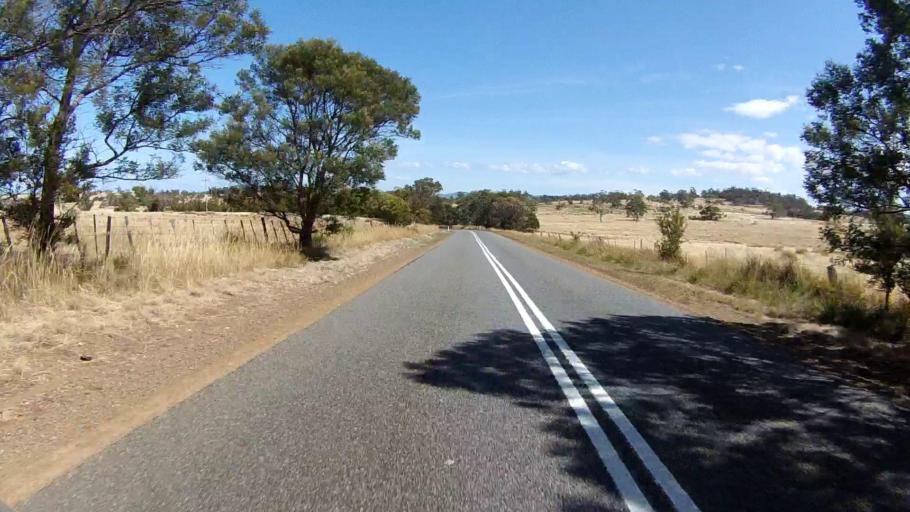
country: AU
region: Tasmania
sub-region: Sorell
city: Sorell
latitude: -42.2911
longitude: 147.9916
